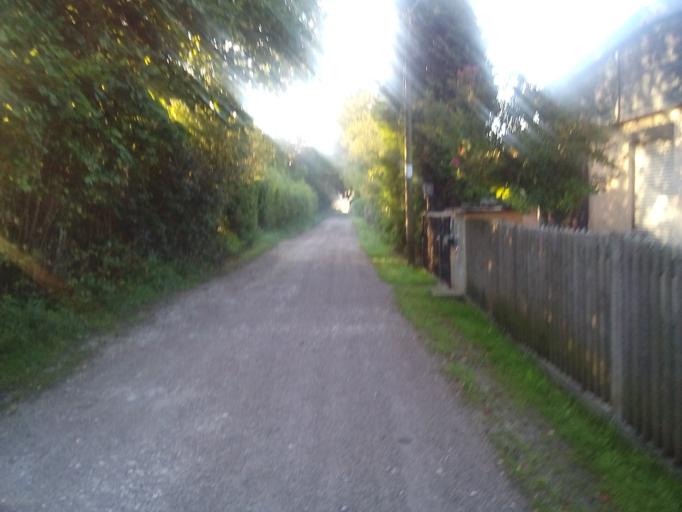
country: DE
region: Bavaria
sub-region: Upper Bavaria
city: Unterfoehring
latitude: 48.1664
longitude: 11.6638
